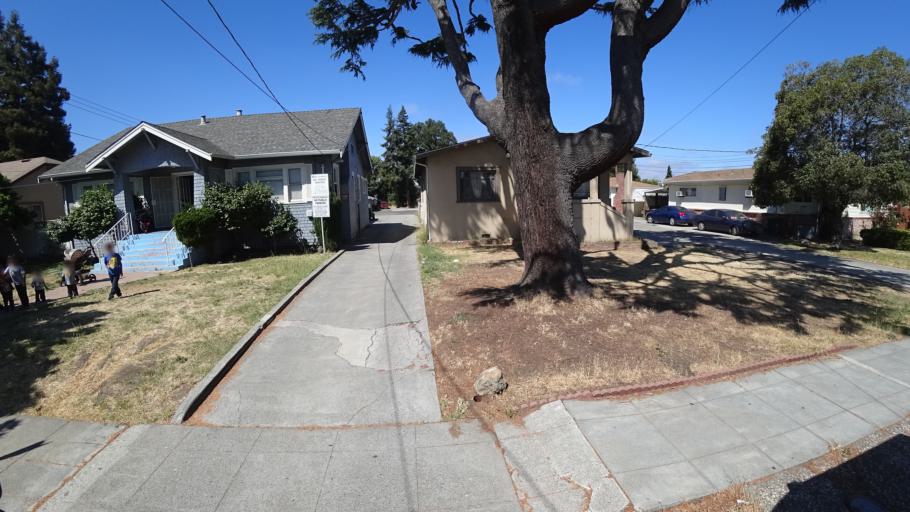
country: US
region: California
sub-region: Alameda County
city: Hayward
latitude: 37.6748
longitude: -122.0913
